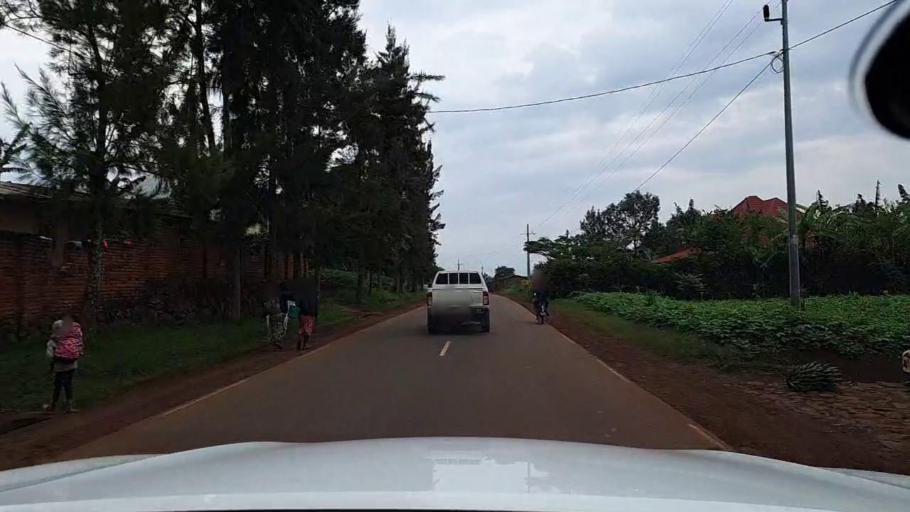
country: RW
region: Western Province
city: Cyangugu
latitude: -2.6201
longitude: 28.9458
